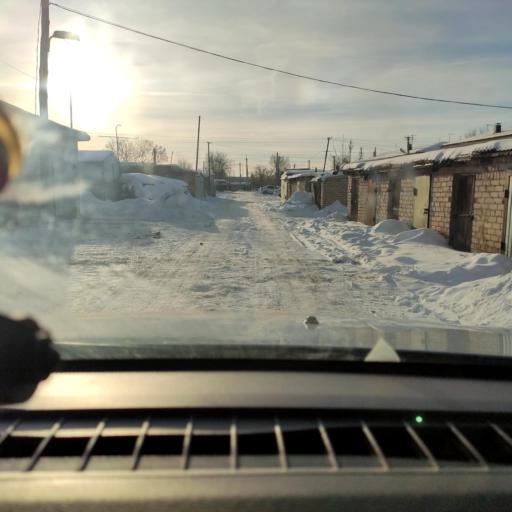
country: RU
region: Samara
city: Samara
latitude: 53.1370
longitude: 50.2410
